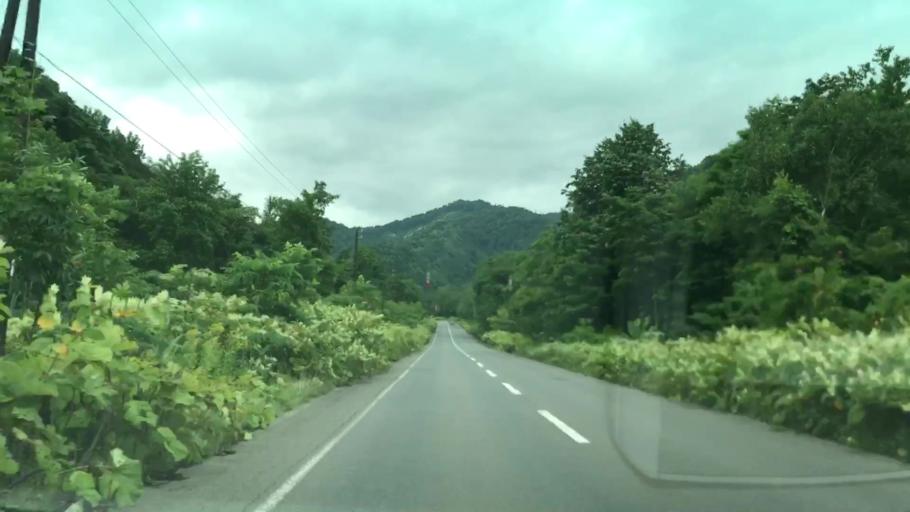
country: JP
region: Hokkaido
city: Yoichi
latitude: 43.0177
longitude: 140.8678
